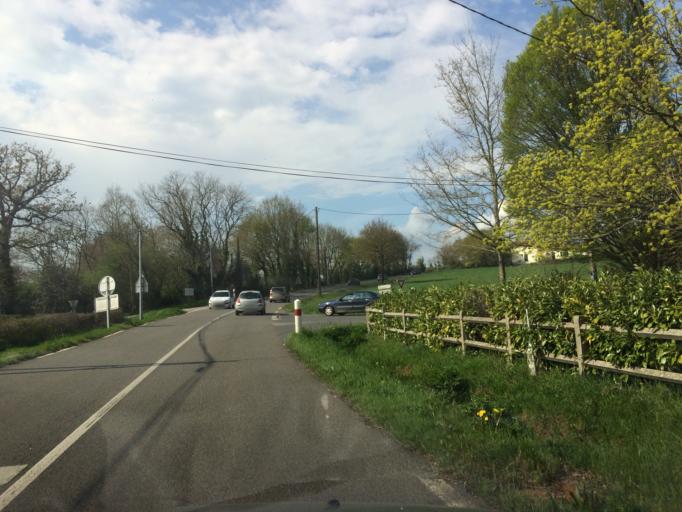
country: FR
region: Pays de la Loire
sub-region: Departement de la Loire-Atlantique
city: Carquefou
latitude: 47.3168
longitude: -1.5098
